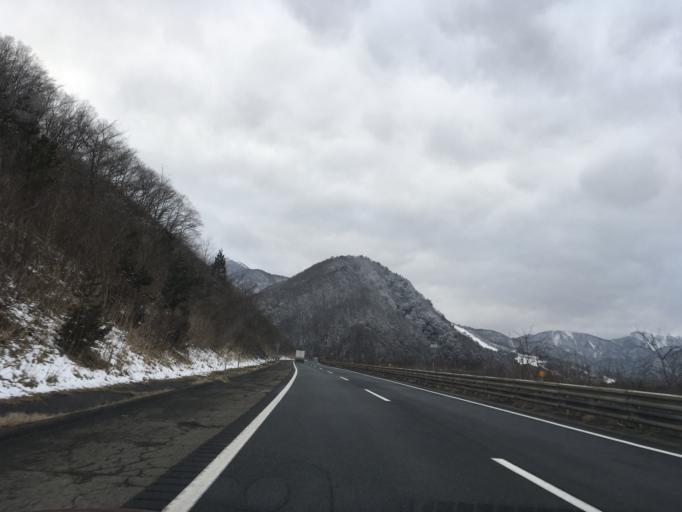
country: JP
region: Yamagata
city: Yamagata-shi
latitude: 38.2125
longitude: 140.5366
